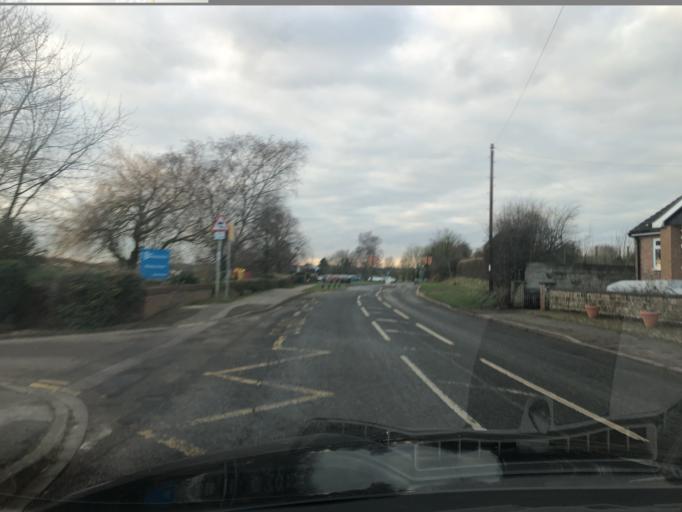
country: GB
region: England
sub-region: North Yorkshire
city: Bedale
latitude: 54.2841
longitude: -1.5986
